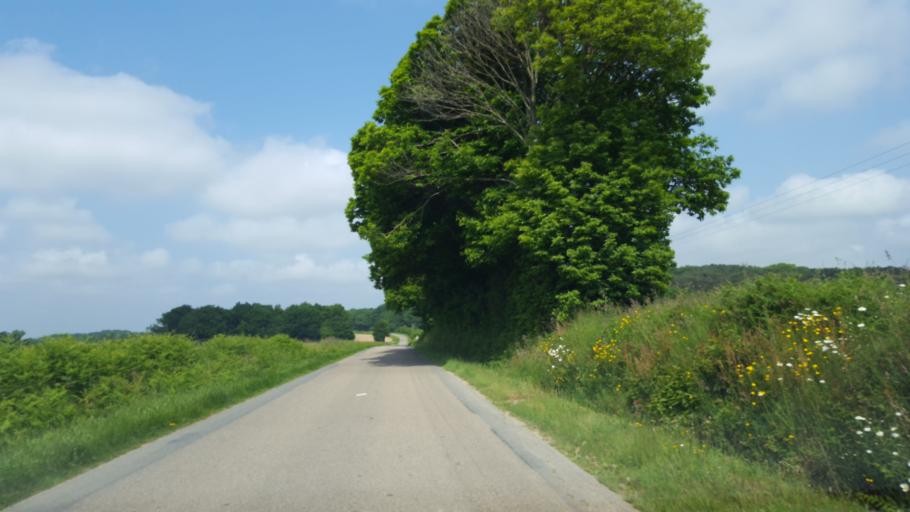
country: FR
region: Brittany
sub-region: Departement d'Ille-et-Vilaine
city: Guignen
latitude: 47.9255
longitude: -1.8904
